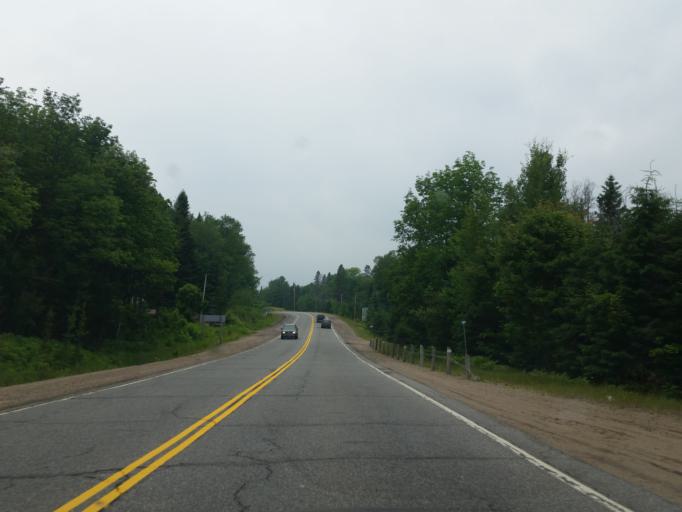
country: CA
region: Ontario
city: Huntsville
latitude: 45.3672
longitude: -79.1277
